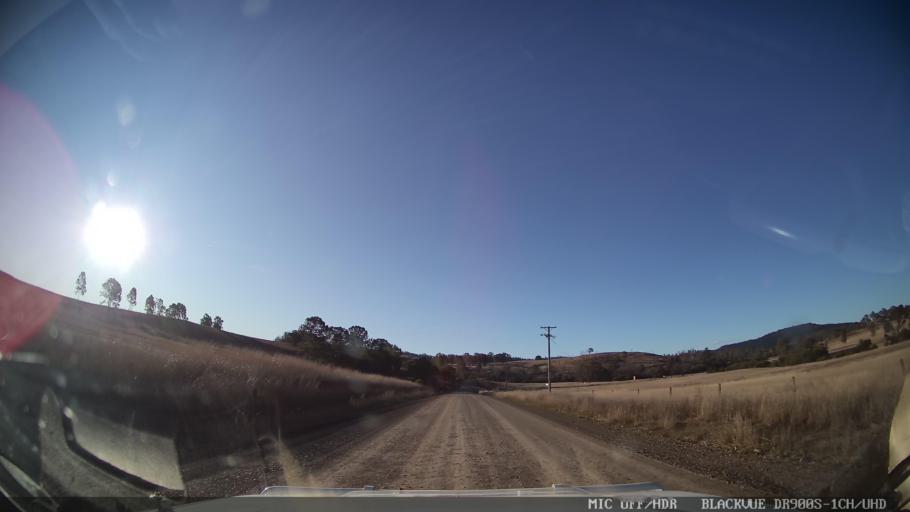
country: AU
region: Queensland
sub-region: Gladstone
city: Toolooa
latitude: -24.6919
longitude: 151.3063
